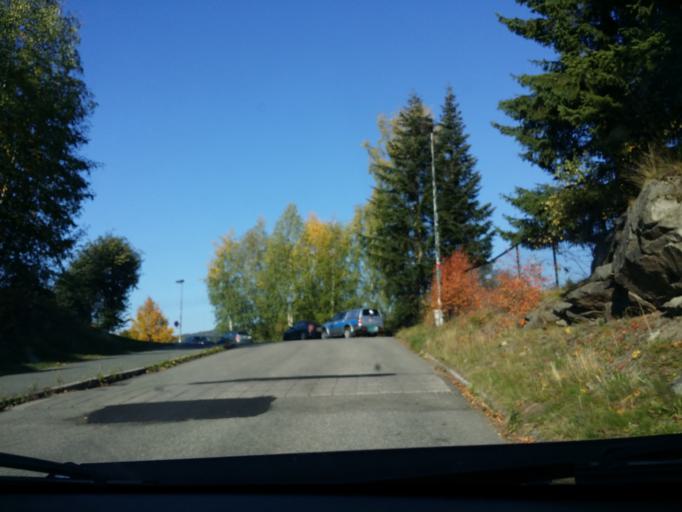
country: NO
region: Akershus
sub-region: Baerum
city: Skui
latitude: 59.9451
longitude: 10.5035
